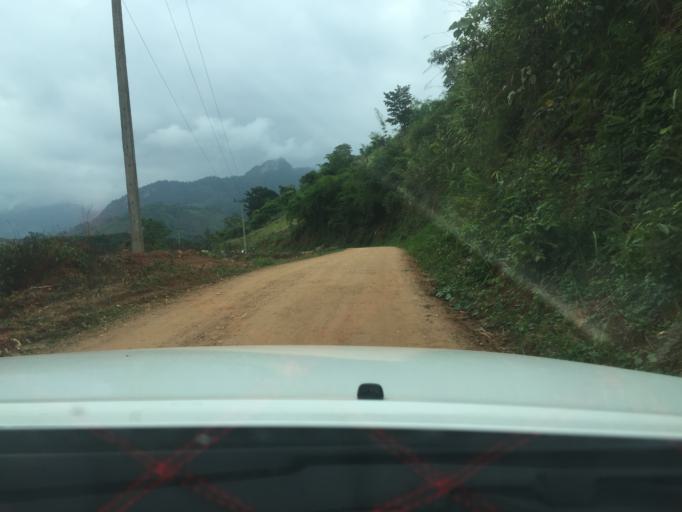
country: TH
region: Phayao
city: Phu Sang
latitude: 19.7338
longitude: 100.4786
